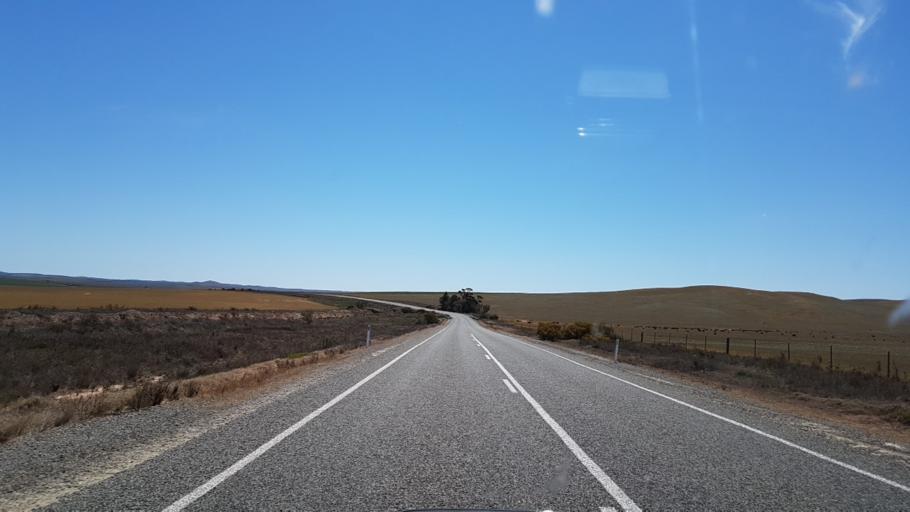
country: AU
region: South Australia
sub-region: Northern Areas
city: Jamestown
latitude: -33.3143
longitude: 138.8825
